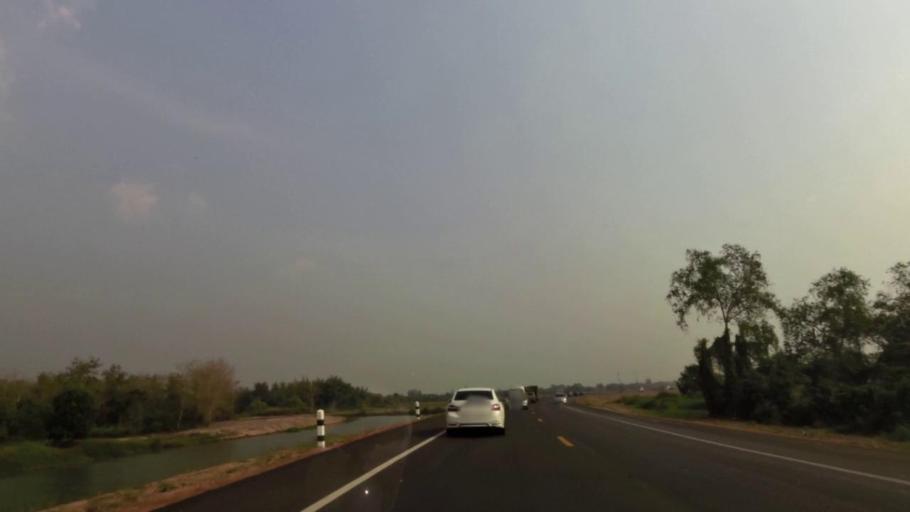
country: TH
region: Rayong
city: Klaeng
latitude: 12.7943
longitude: 101.6721
